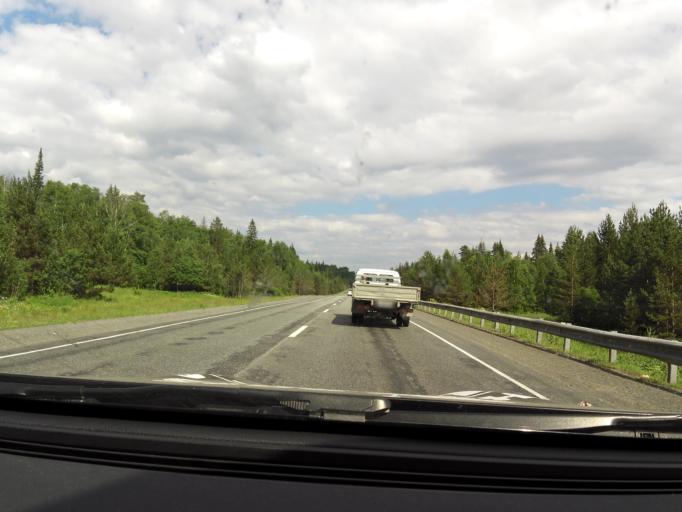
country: RU
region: Sverdlovsk
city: Nizhniye Sergi
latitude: 56.8249
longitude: 59.2638
